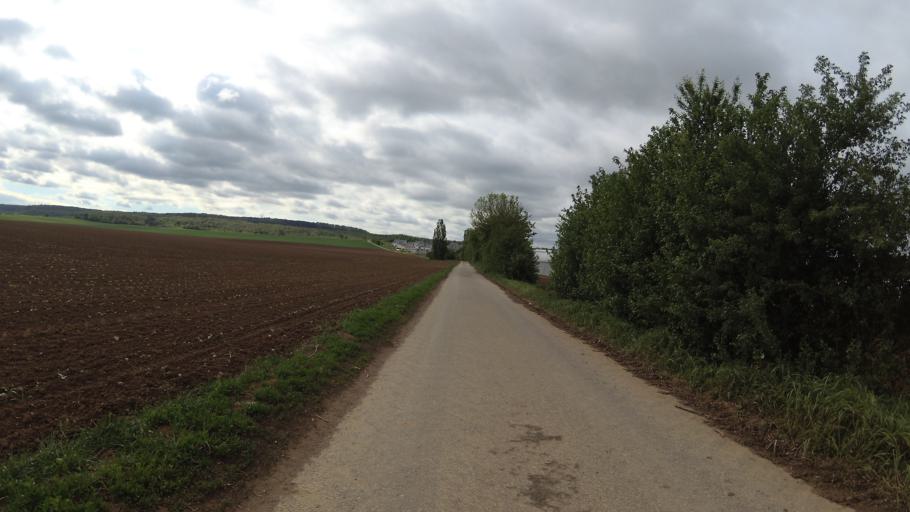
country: DE
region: Baden-Wuerttemberg
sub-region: Regierungsbezirk Stuttgart
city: Oedheim
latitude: 49.2165
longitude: 9.2614
